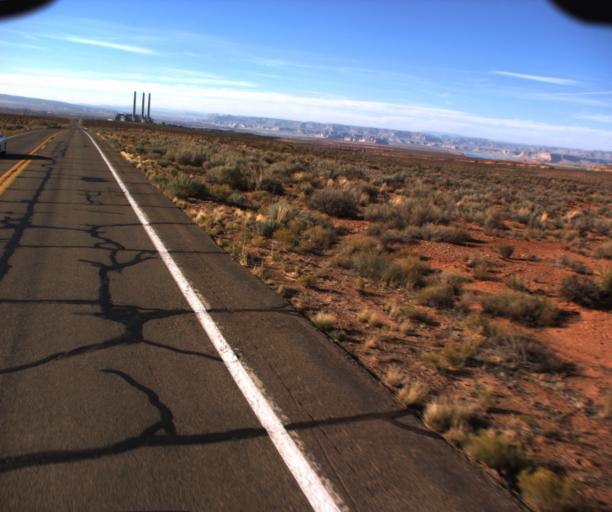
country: US
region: Arizona
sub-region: Coconino County
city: LeChee
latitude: 36.8799
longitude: -111.3470
